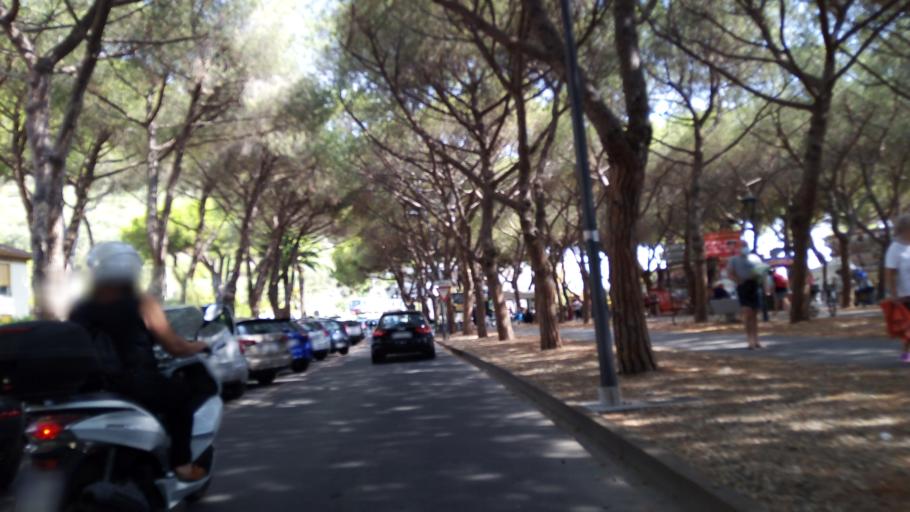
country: IT
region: Liguria
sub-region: Provincia di Savona
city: Ceriale
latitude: 44.0991
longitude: 8.2354
